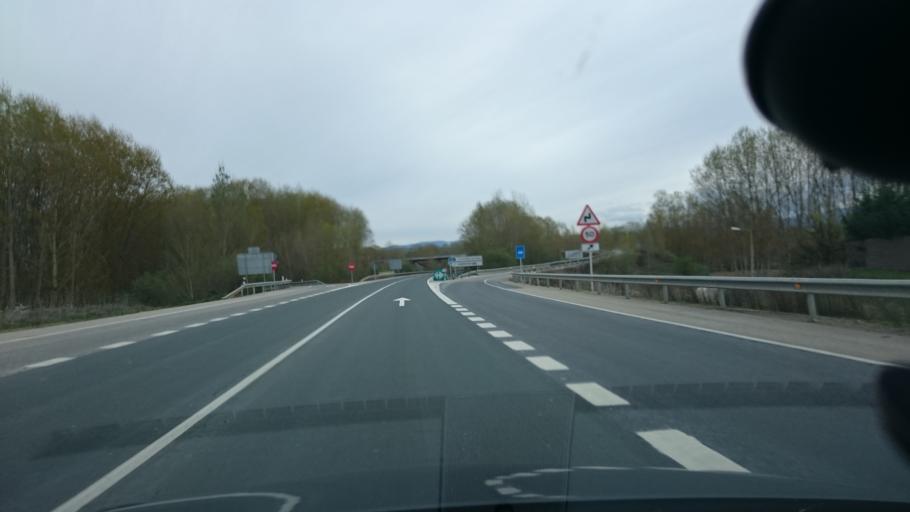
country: ES
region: Castille and Leon
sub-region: Provincia de Leon
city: Villadecanes
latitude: 42.5687
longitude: -6.7466
